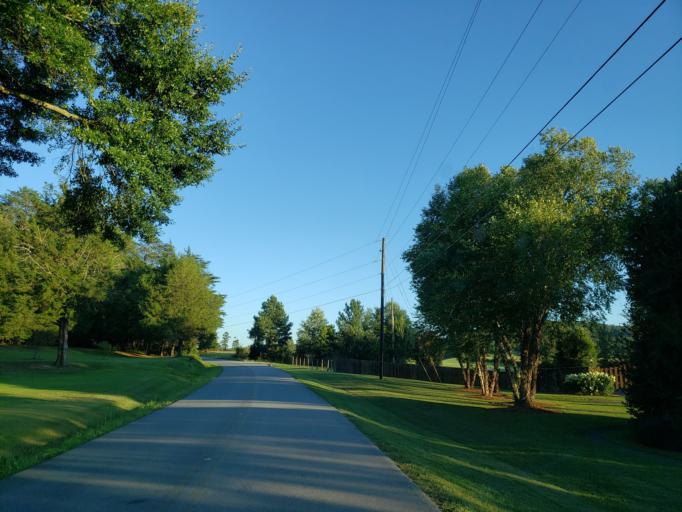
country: US
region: Georgia
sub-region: Bartow County
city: Euharlee
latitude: 34.0796
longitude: -84.9774
